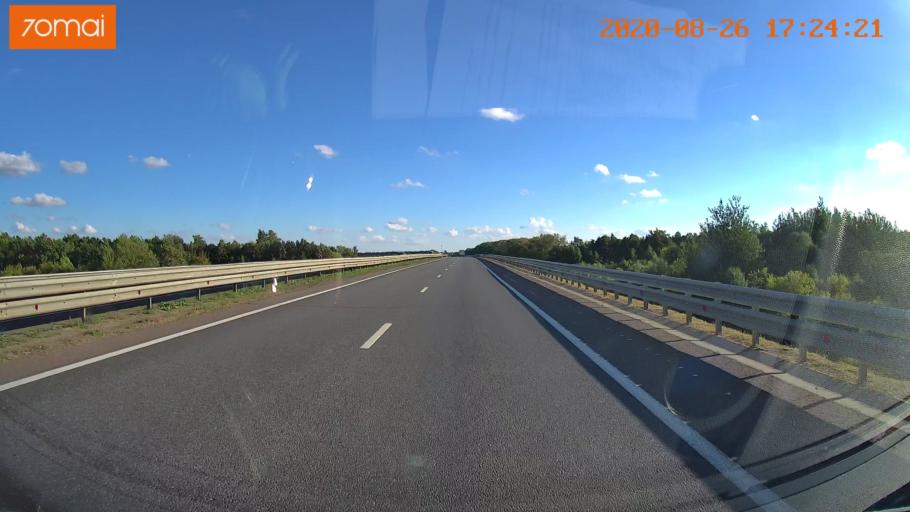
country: RU
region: Tula
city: Volovo
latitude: 53.5193
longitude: 38.1163
